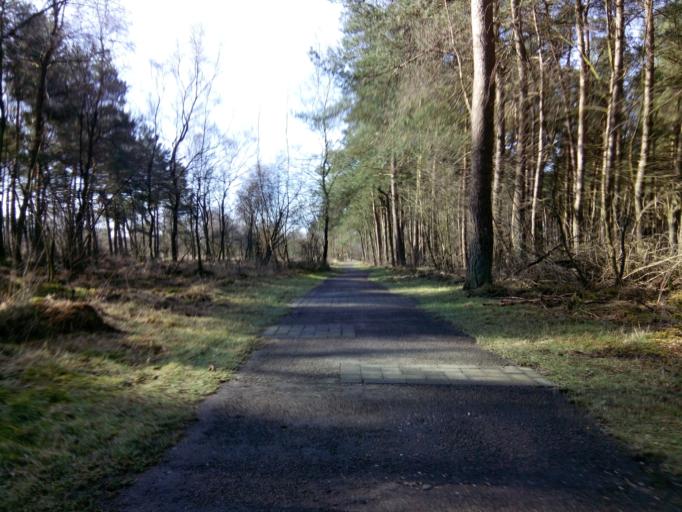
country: NL
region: Gelderland
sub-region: Gemeente Apeldoorn
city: Uddel
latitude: 52.1978
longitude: 5.8130
